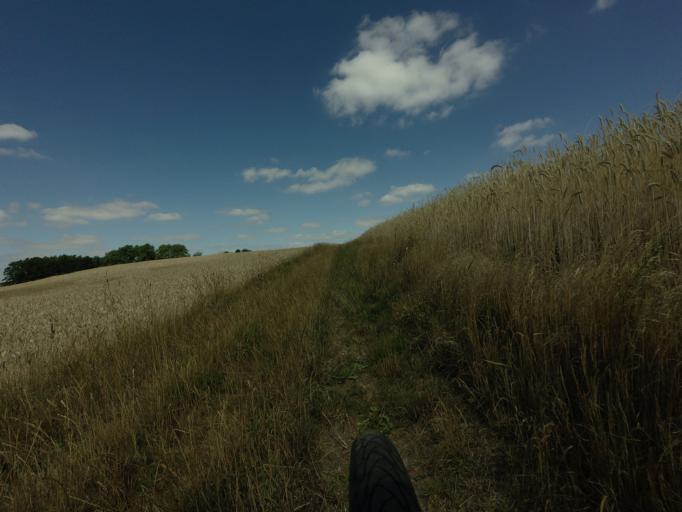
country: DK
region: Central Jutland
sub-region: Odder Kommune
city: Odder
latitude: 55.8950
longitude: 10.0719
